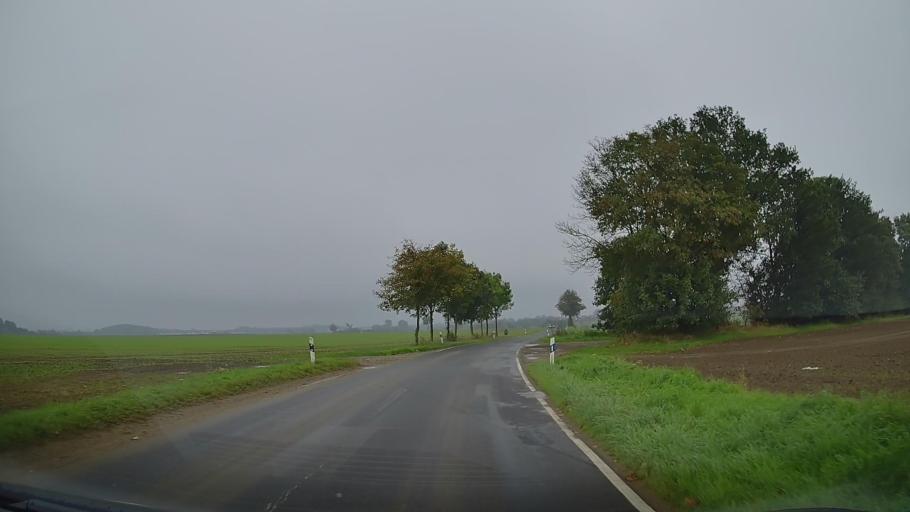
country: DE
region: Mecklenburg-Vorpommern
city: Wismar
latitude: 53.9162
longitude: 11.3935
